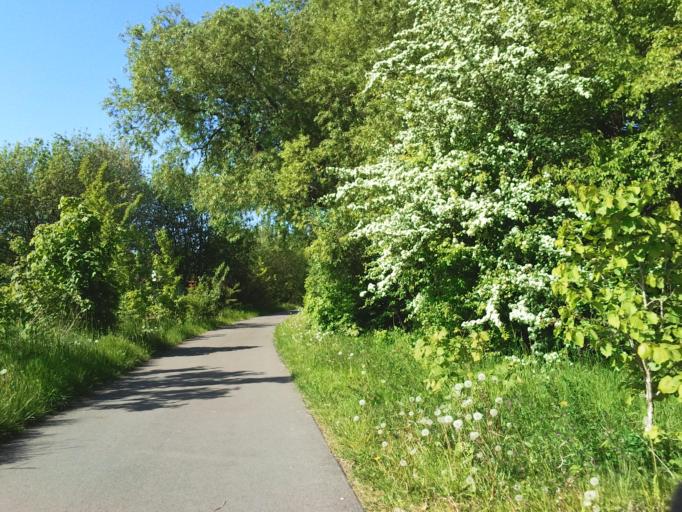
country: DE
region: Mecklenburg-Vorpommern
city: Nienhagen
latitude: 54.1280
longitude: 12.1728
